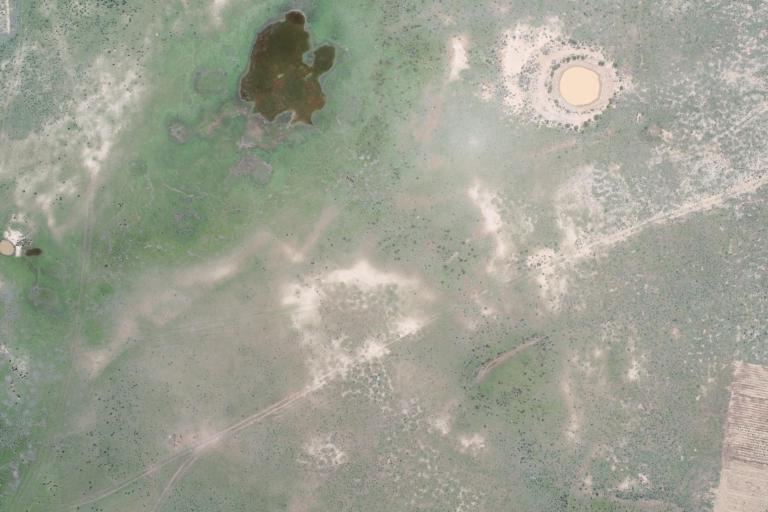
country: BO
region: La Paz
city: Curahuara de Carangas
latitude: -17.3115
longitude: -68.5168
